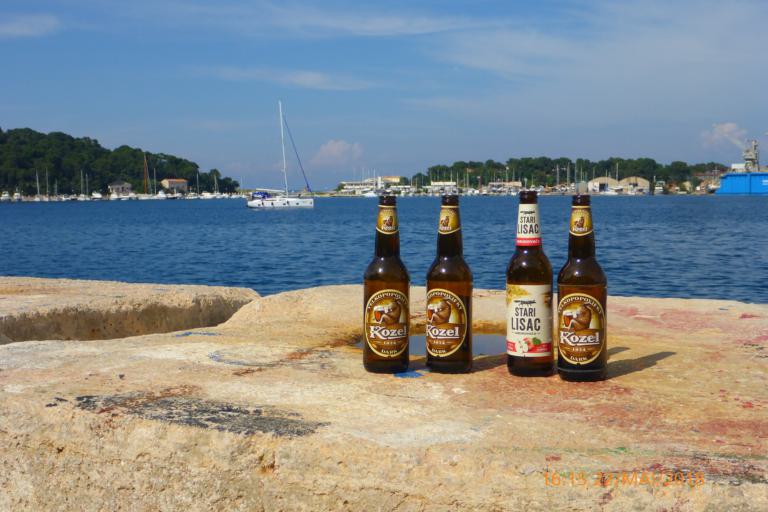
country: HR
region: Primorsko-Goranska
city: Mali Losinj
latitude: 44.5407
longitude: 14.4534
